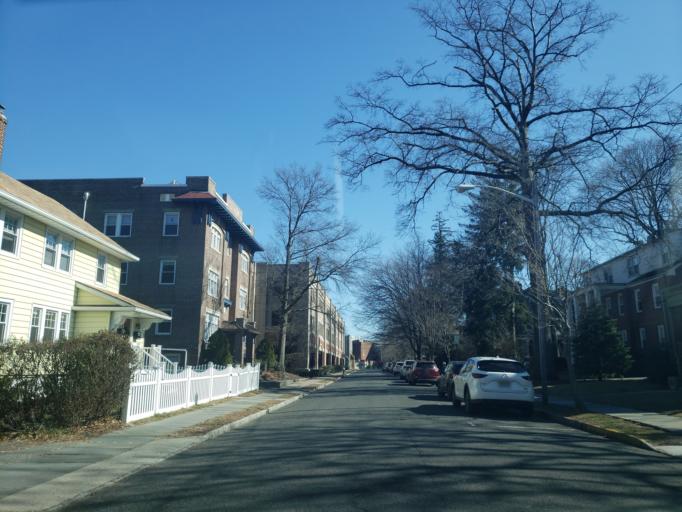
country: US
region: New Jersey
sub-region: Essex County
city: Montclair
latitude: 40.8131
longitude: -74.2199
